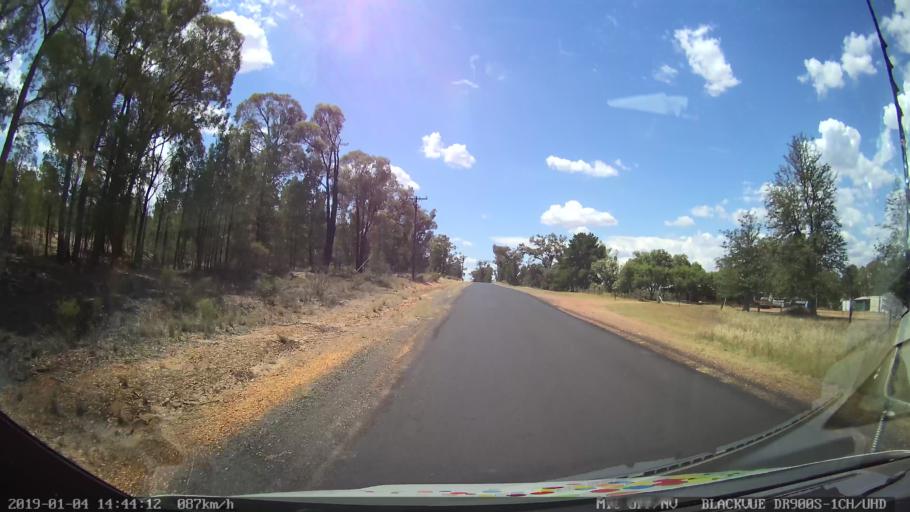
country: AU
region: New South Wales
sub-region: Dubbo Municipality
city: Dubbo
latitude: -32.1092
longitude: 148.6551
